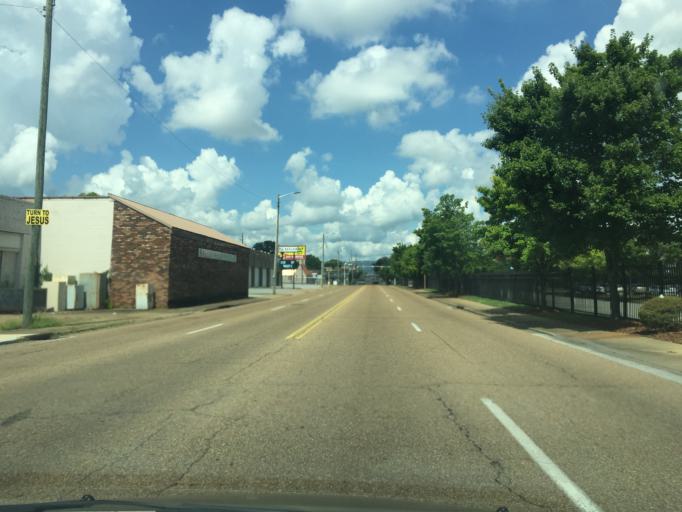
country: US
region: Tennessee
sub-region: Hamilton County
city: East Ridge
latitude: 35.0331
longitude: -85.2671
